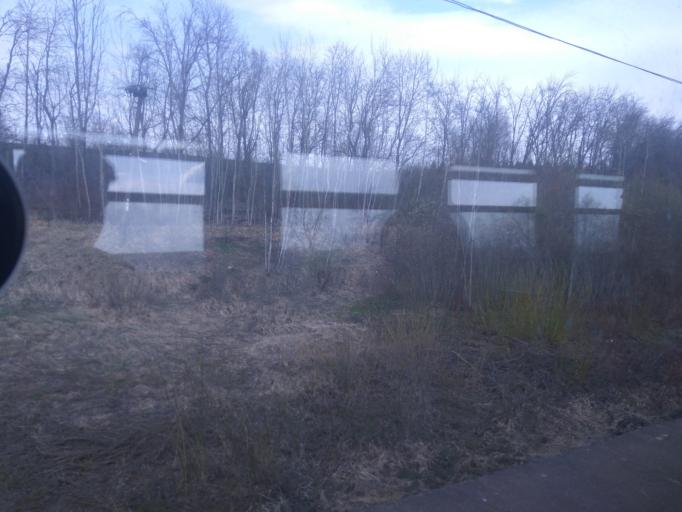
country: RU
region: Moskovskaya
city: Budenovetc
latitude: 56.3100
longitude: 37.6633
